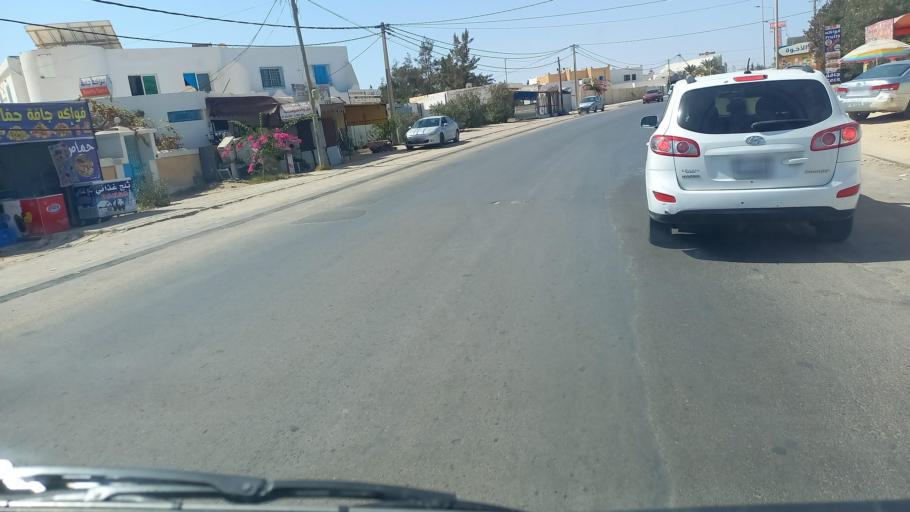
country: TN
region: Madanin
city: Houmt Souk
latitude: 33.8723
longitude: 10.8736
